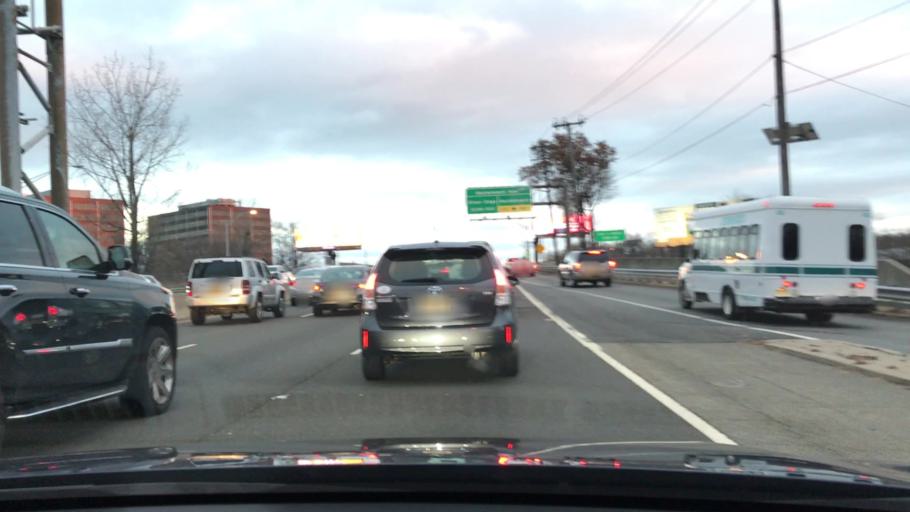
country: US
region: New Jersey
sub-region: Bergen County
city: River Edge
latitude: 40.9100
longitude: -74.0378
